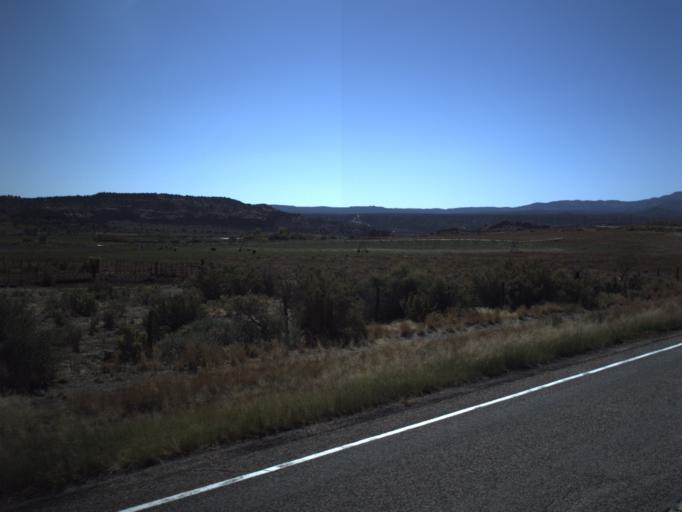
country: US
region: Utah
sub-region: Garfield County
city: Panguitch
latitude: 37.5626
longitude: -112.0110
